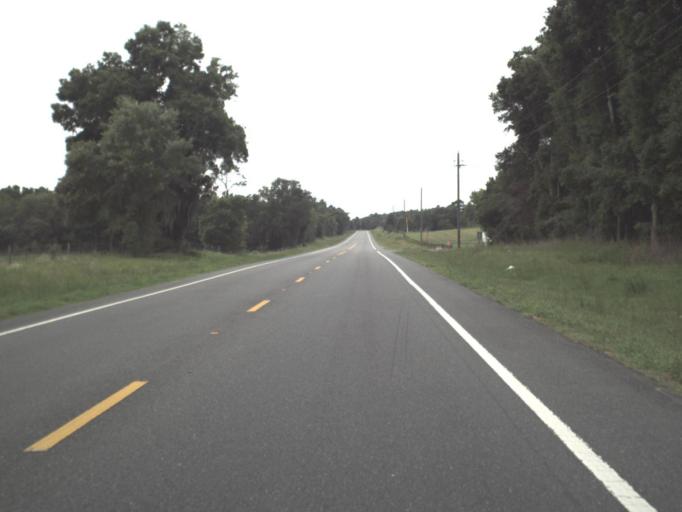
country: US
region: Florida
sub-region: Levy County
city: Williston Highlands
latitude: 29.2281
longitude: -82.4411
